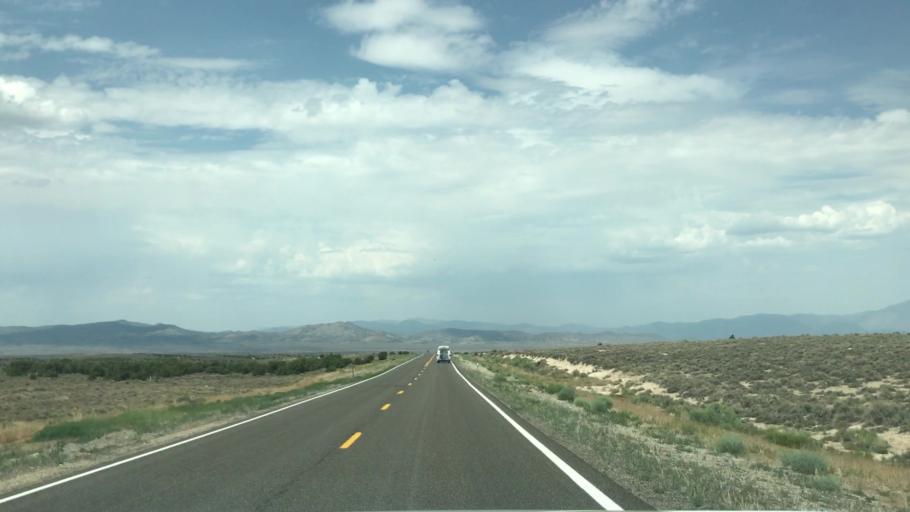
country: US
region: Nevada
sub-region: Eureka County
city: Eureka
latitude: 39.3928
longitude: -115.5151
